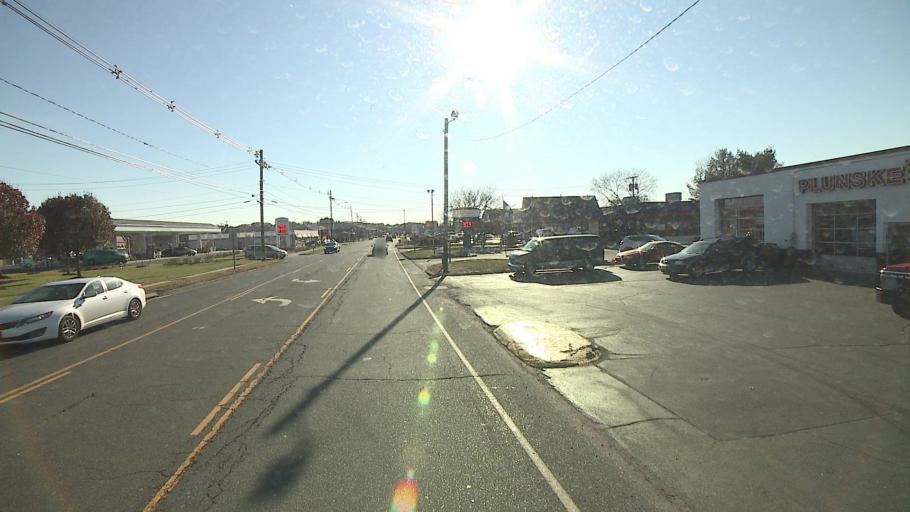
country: US
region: Connecticut
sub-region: New Haven County
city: Wallingford
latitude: 41.4837
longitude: -72.8099
